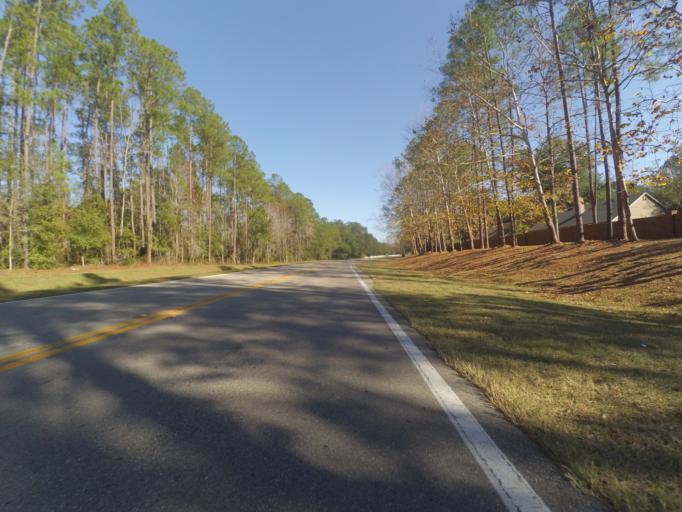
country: US
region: Florida
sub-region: Alachua County
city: Gainesville
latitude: 29.6101
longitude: -82.4288
